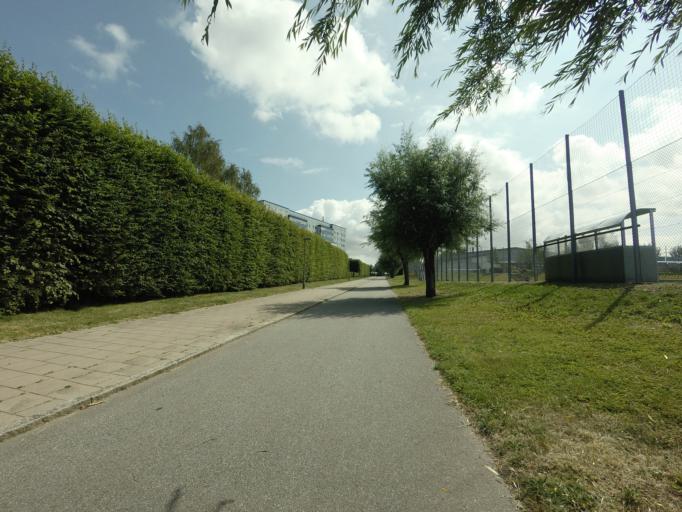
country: SE
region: Skane
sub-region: Malmo
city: Malmoe
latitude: 55.5715
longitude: 13.0002
